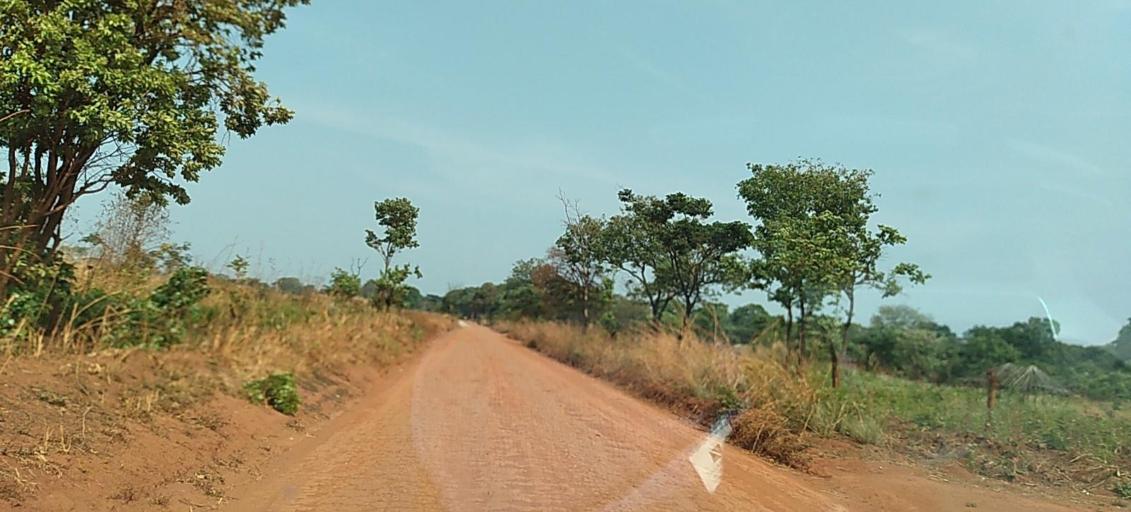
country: ZM
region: Copperbelt
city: Chililabombwe
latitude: -12.3423
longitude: 27.7004
